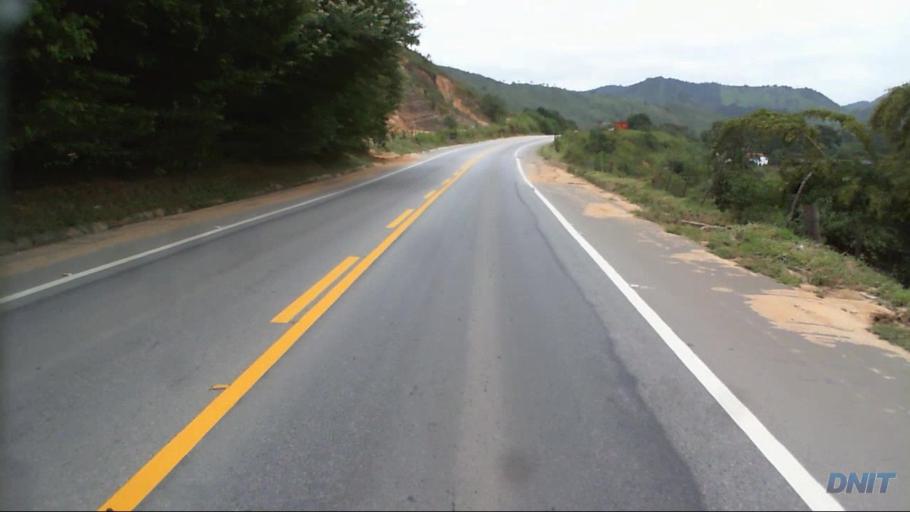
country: BR
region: Minas Gerais
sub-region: Timoteo
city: Timoteo
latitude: -19.6119
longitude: -42.7680
